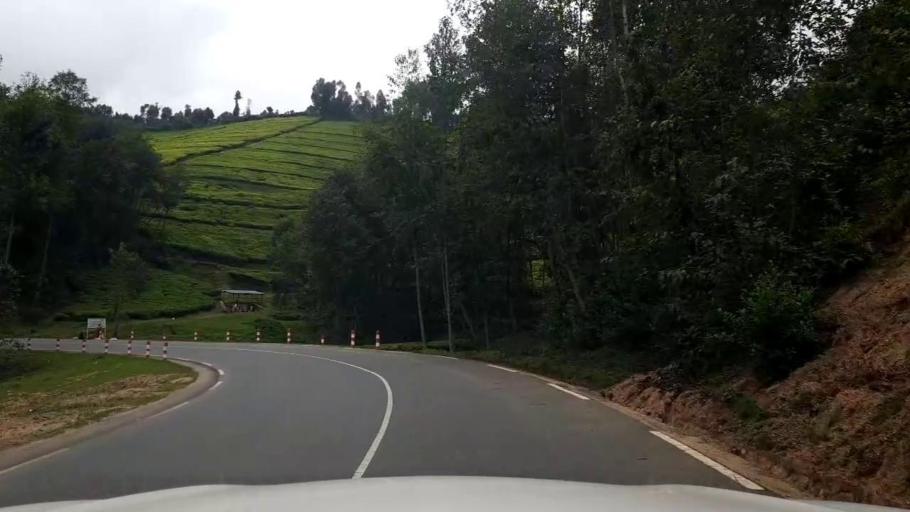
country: RW
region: Northern Province
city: Musanze
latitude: -1.6551
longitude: 29.5095
